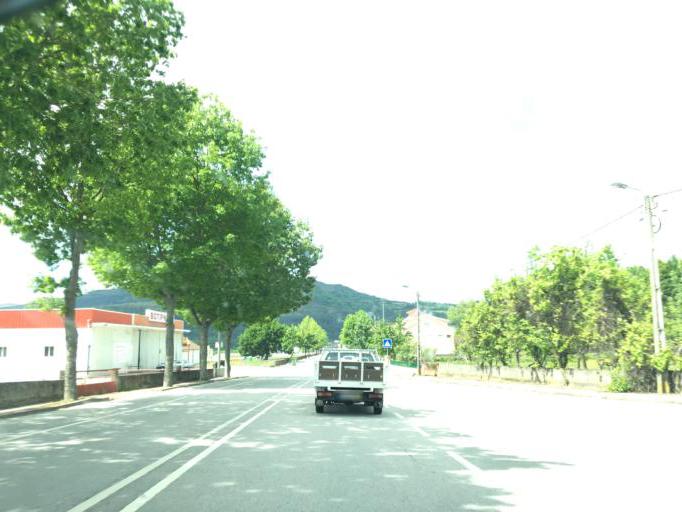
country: PT
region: Vila Real
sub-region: Boticas
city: Boticas
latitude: 41.6934
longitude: -7.6537
